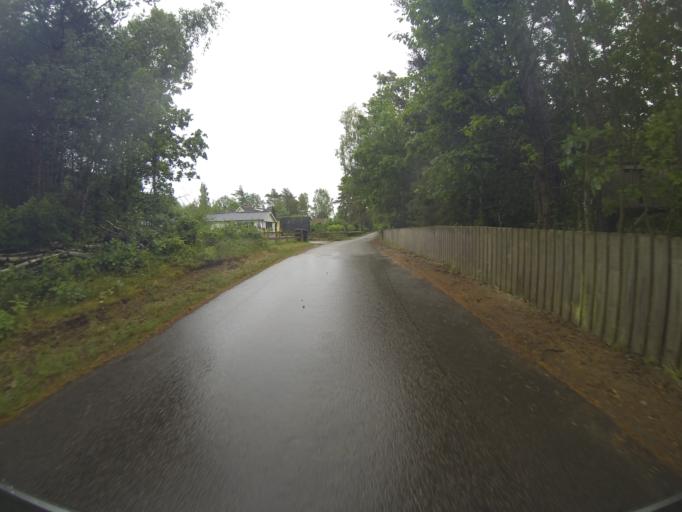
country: SE
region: Blekinge
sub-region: Ronneby Kommun
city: Ronneby
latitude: 56.1717
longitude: 15.3098
